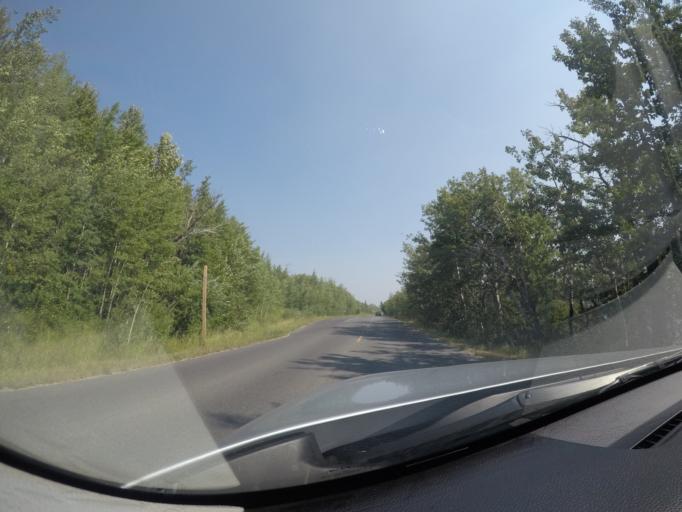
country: US
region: Montana
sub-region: Glacier County
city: North Browning
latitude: 48.7398
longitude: -113.4568
